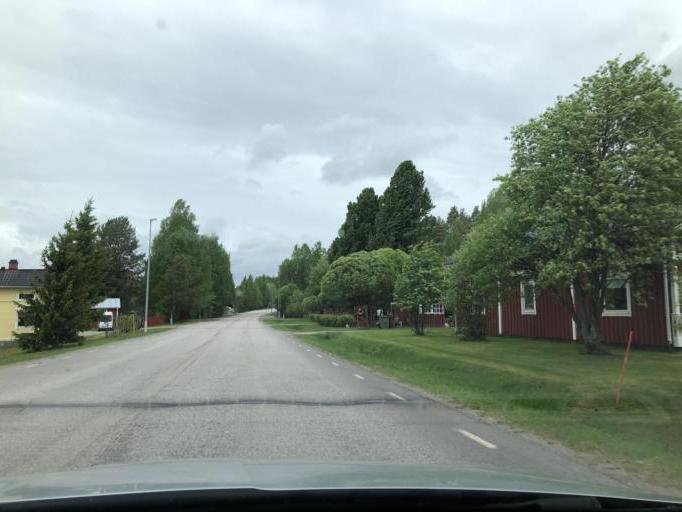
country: SE
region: Norrbotten
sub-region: Pitea Kommun
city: Bergsviken
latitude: 65.3844
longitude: 21.3313
